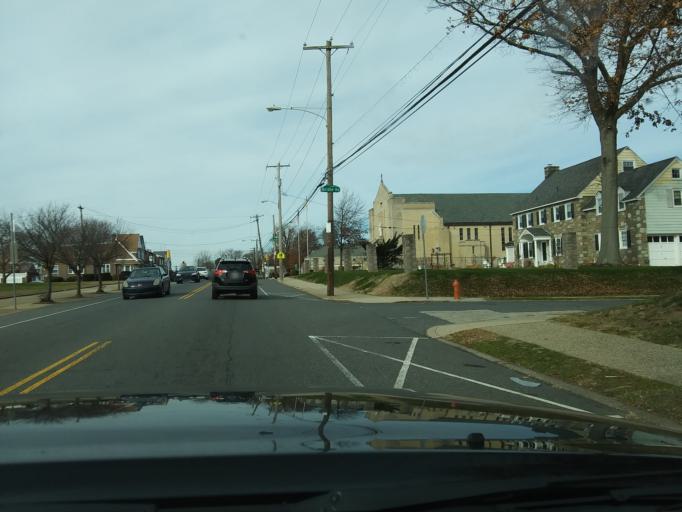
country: US
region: Pennsylvania
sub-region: Montgomery County
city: Rockledge
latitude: 40.0754
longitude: -75.0799
